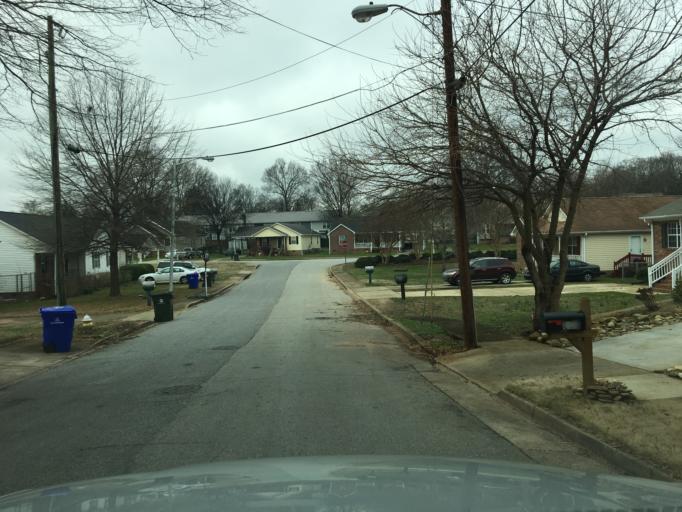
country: US
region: South Carolina
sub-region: Greenville County
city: Greenville
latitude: 34.8573
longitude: -82.4103
